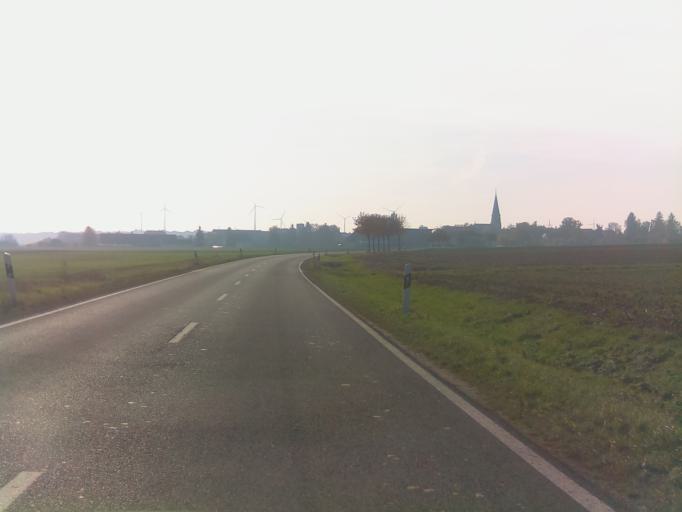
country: DE
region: Bavaria
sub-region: Regierungsbezirk Unterfranken
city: Biebelried
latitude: 49.7513
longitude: 10.0702
